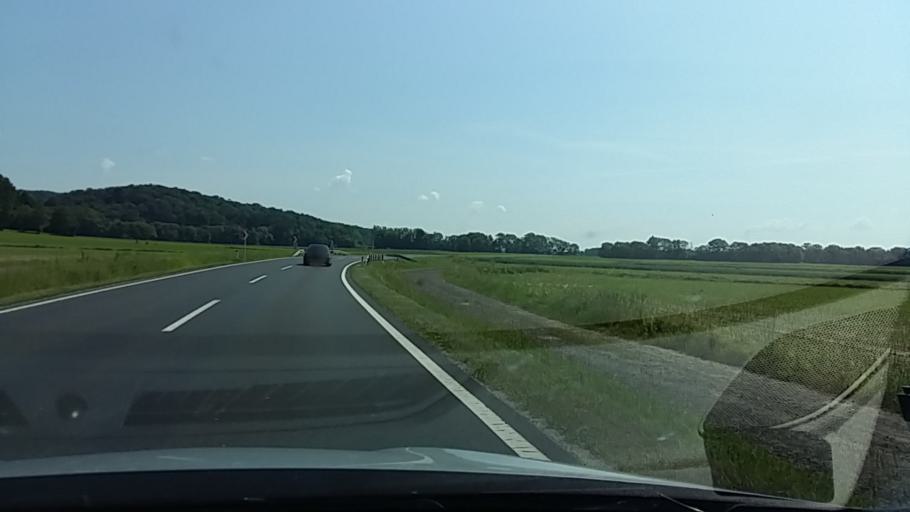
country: AT
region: Burgenland
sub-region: Politischer Bezirk Jennersdorf
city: Weichselbaum
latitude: 46.9451
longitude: 16.1996
